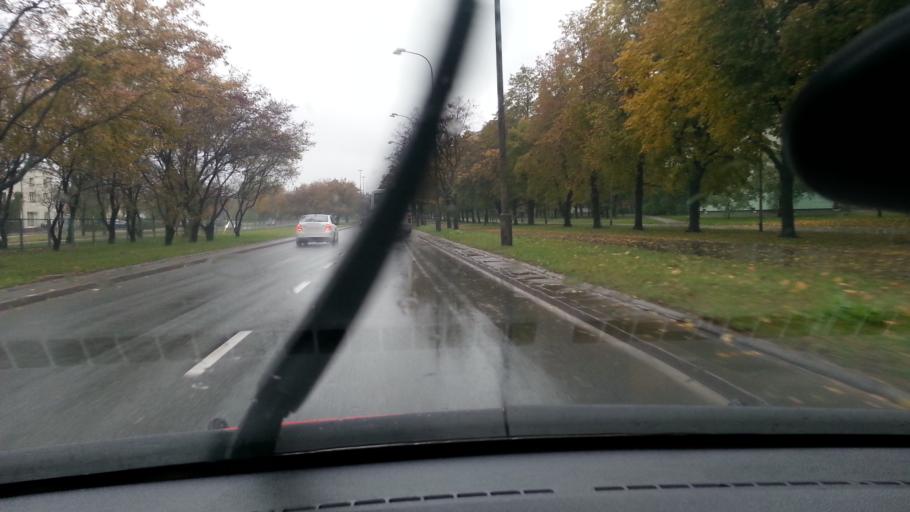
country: PL
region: Masovian Voivodeship
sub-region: Warszawa
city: Targowek
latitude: 52.2883
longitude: 21.0206
